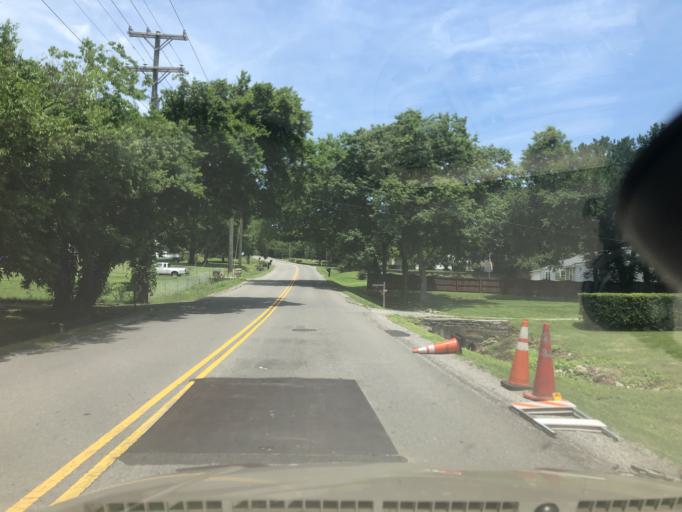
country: US
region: Tennessee
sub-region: Davidson County
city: Lakewood
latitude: 36.2573
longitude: -86.6919
